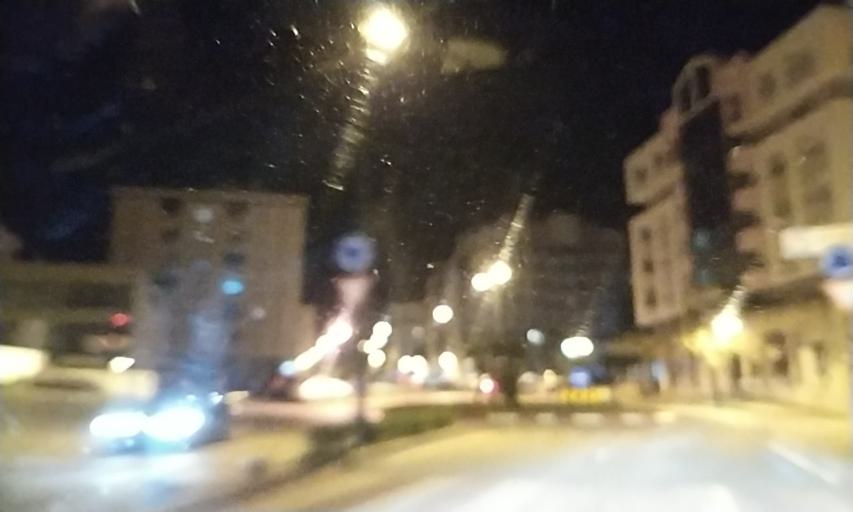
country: PT
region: Castelo Branco
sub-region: Concelho do Fundao
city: Fundao
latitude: 40.1410
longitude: -7.5049
